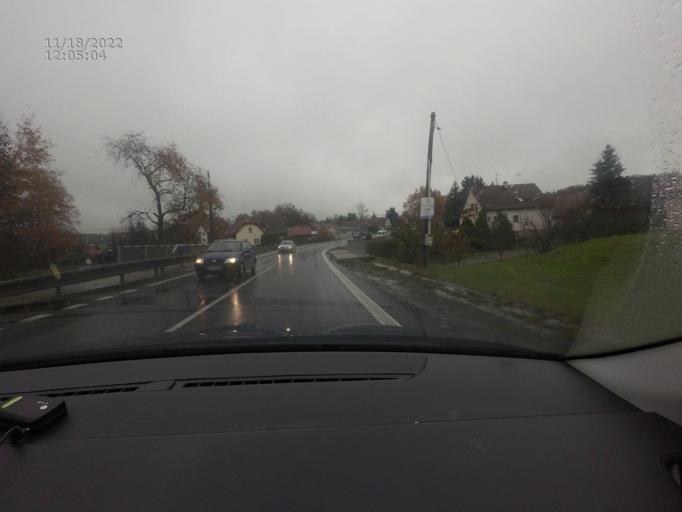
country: CZ
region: Plzensky
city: Nezvestice
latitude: 49.6283
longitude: 13.4832
